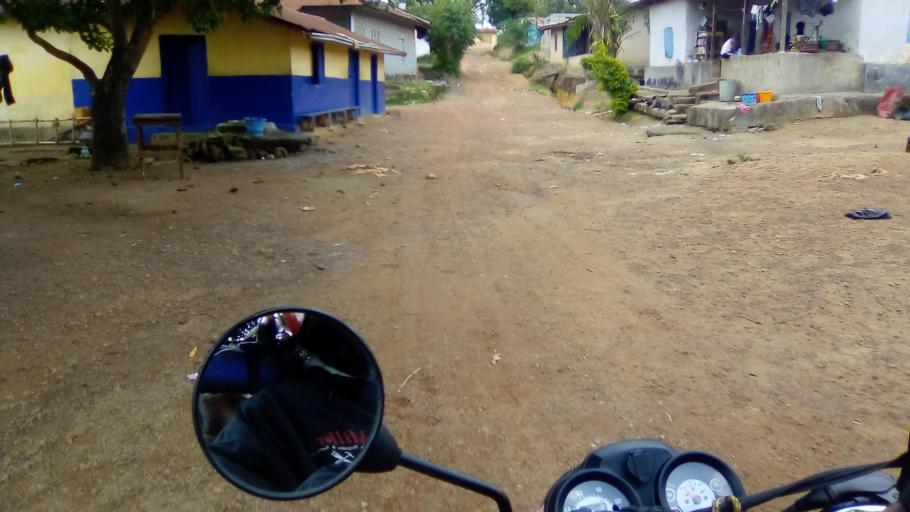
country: SL
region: Southern Province
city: Bo
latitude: 7.9579
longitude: -11.7301
